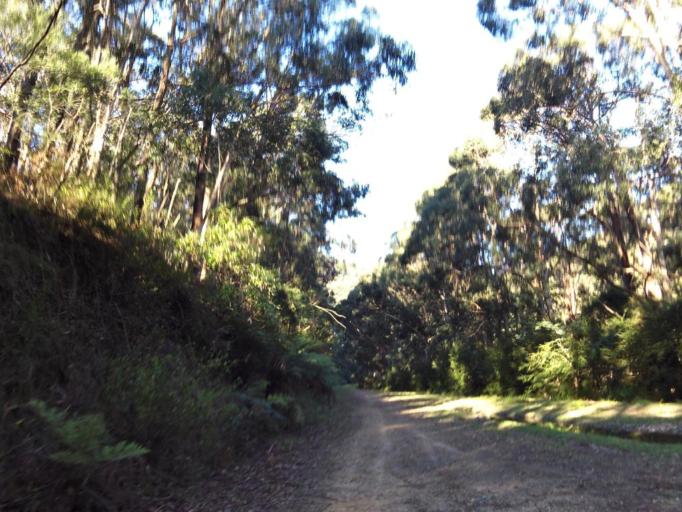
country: AU
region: Victoria
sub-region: Yarra Ranges
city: Millgrove
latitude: -37.7698
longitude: 145.6574
